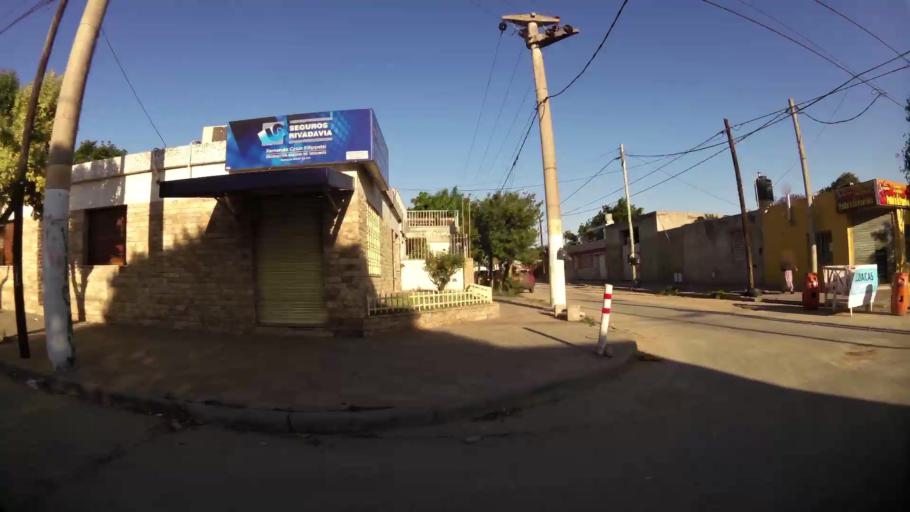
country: AR
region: Cordoba
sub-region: Departamento de Capital
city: Cordoba
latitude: -31.3751
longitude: -64.1962
